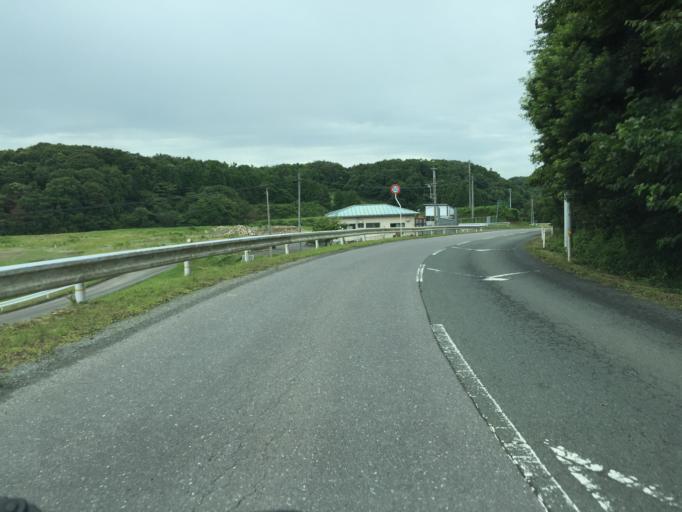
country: JP
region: Fukushima
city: Namie
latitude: 37.7491
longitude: 141.0002
